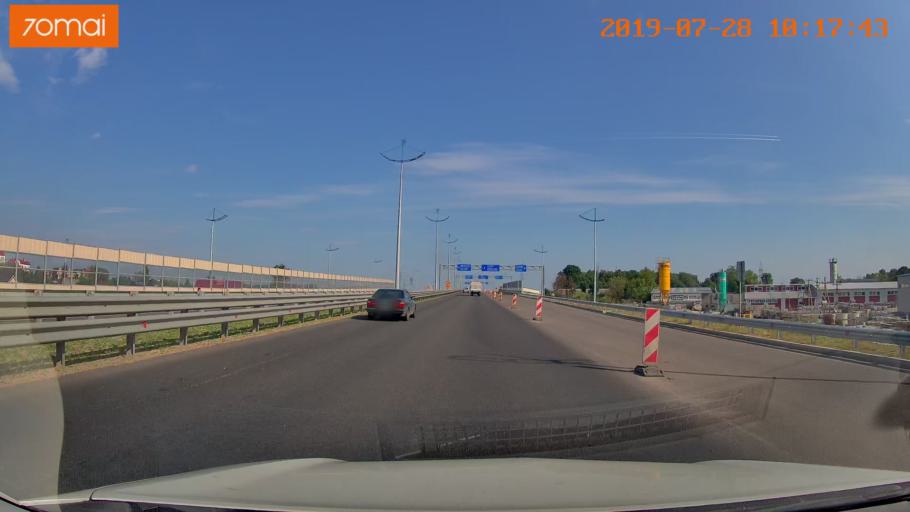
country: RU
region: Kaliningrad
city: Maloye Isakovo
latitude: 54.7435
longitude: 20.5928
